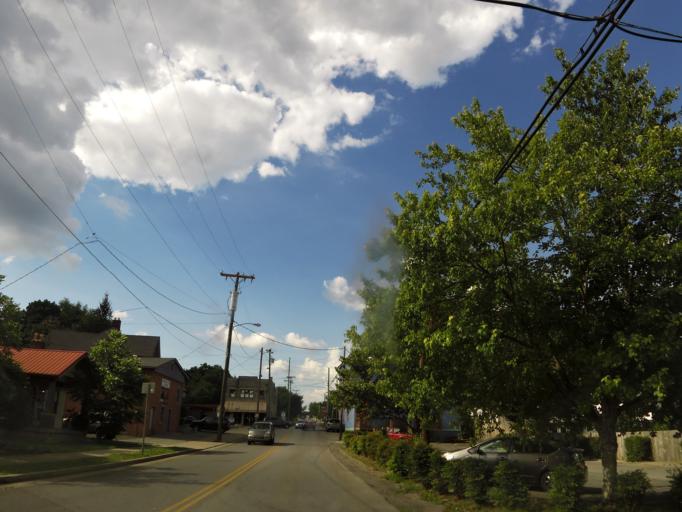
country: US
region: Tennessee
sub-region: Davidson County
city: Nashville
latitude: 36.1764
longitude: -86.7459
